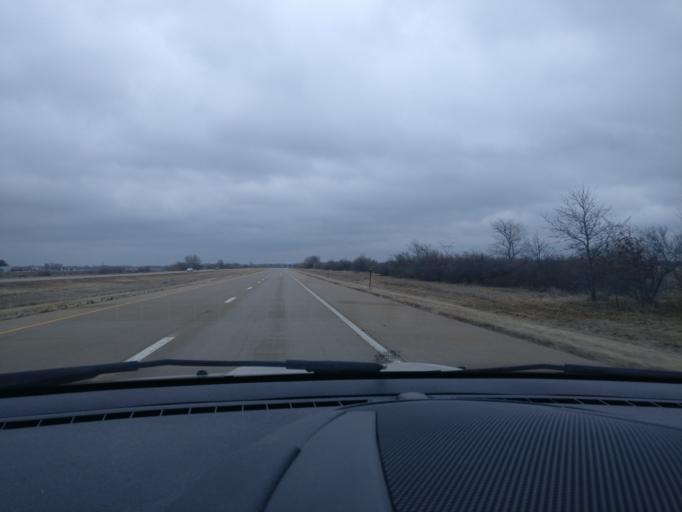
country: US
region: Illinois
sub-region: Whiteside County
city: Sterling
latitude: 41.7653
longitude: -89.8123
